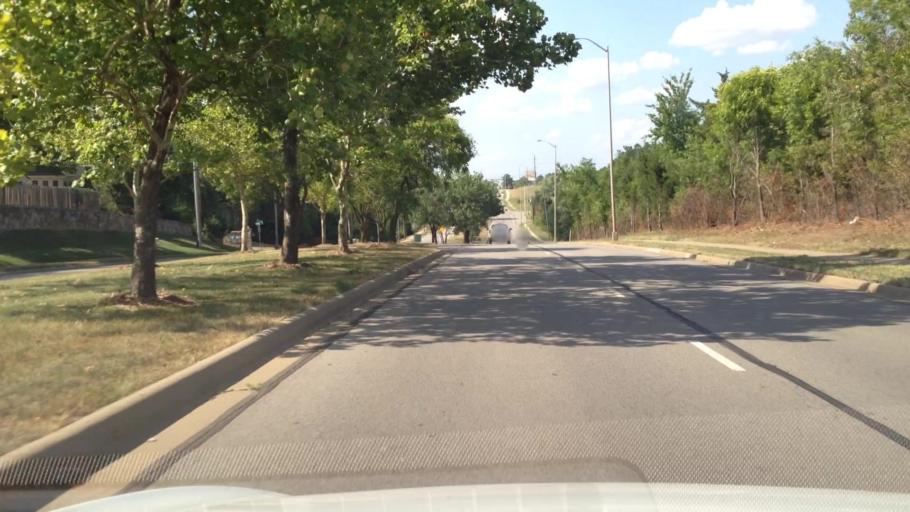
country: US
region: Kansas
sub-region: Johnson County
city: Olathe
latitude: 38.9222
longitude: -94.7973
